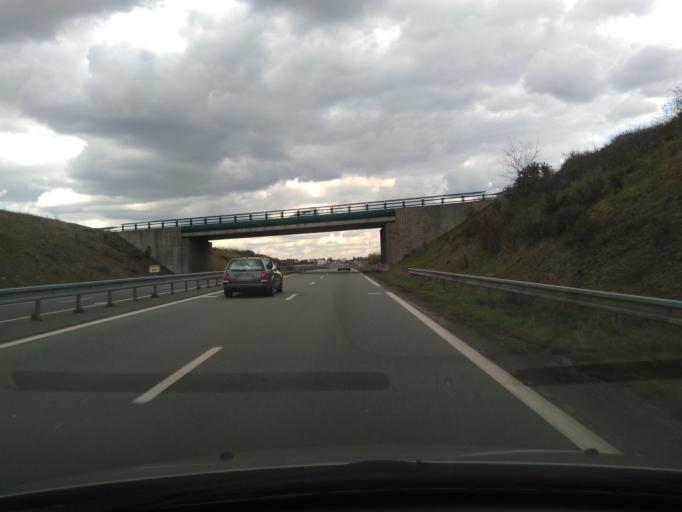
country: FR
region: Pays de la Loire
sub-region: Departement de Maine-et-Loire
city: Saint-Christophe-du-Bois
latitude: 47.0152
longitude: -0.9277
